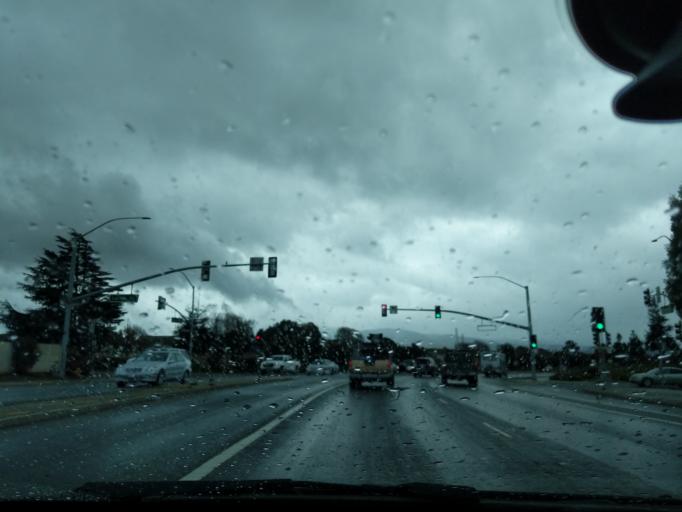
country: US
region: California
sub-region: Monterey County
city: Boronda
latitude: 36.6942
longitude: -121.6685
